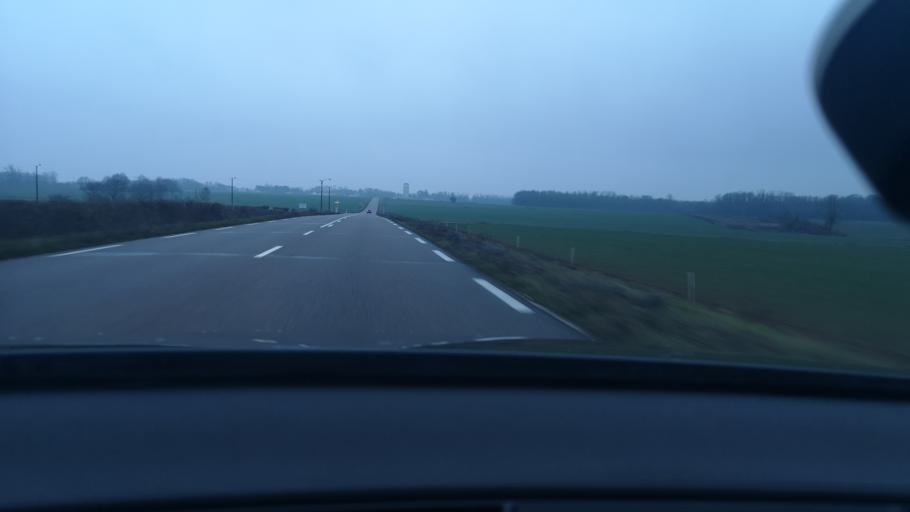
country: FR
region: Bourgogne
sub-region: Departement de la Cote-d'Or
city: Seurre
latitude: 47.0802
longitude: 5.1039
